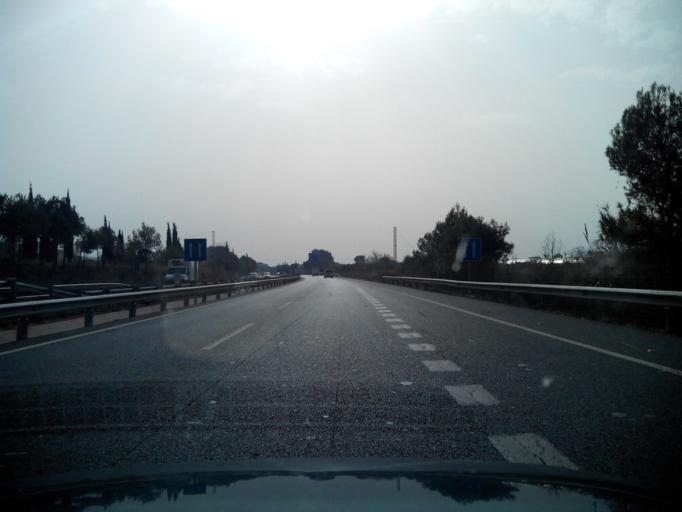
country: ES
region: Catalonia
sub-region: Provincia de Tarragona
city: Reus
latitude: 41.1359
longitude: 1.1014
